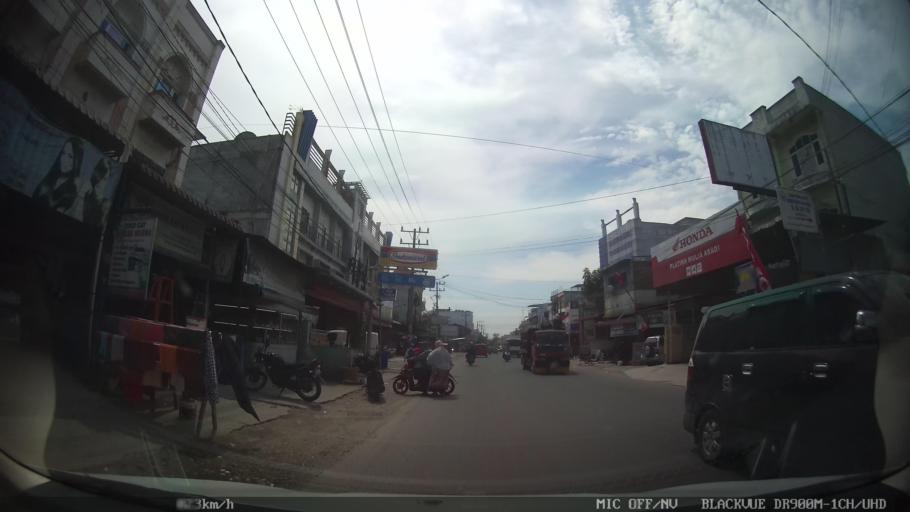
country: ID
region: North Sumatra
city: Labuhan Deli
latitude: 3.6884
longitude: 98.6621
